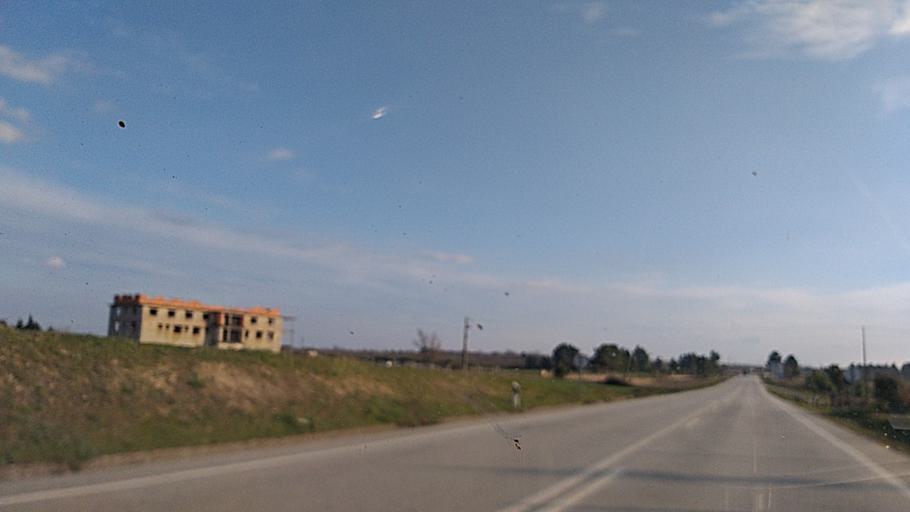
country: ES
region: Castille and Leon
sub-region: Provincia de Salamanca
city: Fuentes de Onoro
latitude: 40.6134
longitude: -6.9820
